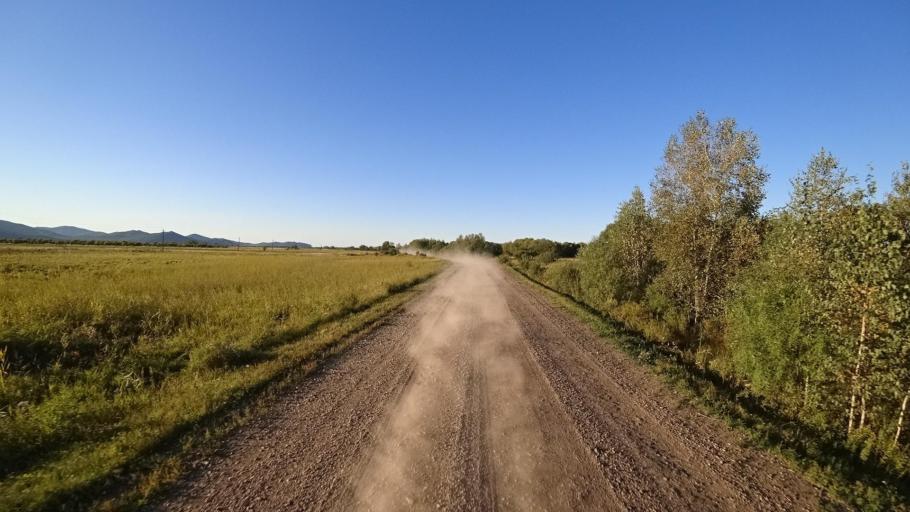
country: RU
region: Primorskiy
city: Kirovskiy
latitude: 44.7887
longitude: 133.6230
